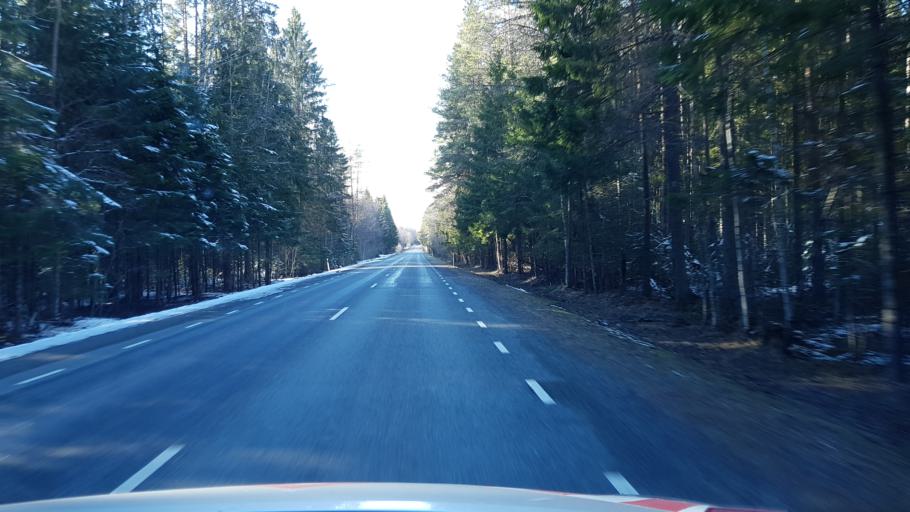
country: EE
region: Laeaene-Virumaa
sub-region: Tapa vald
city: Tapa
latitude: 59.4311
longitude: 25.9726
